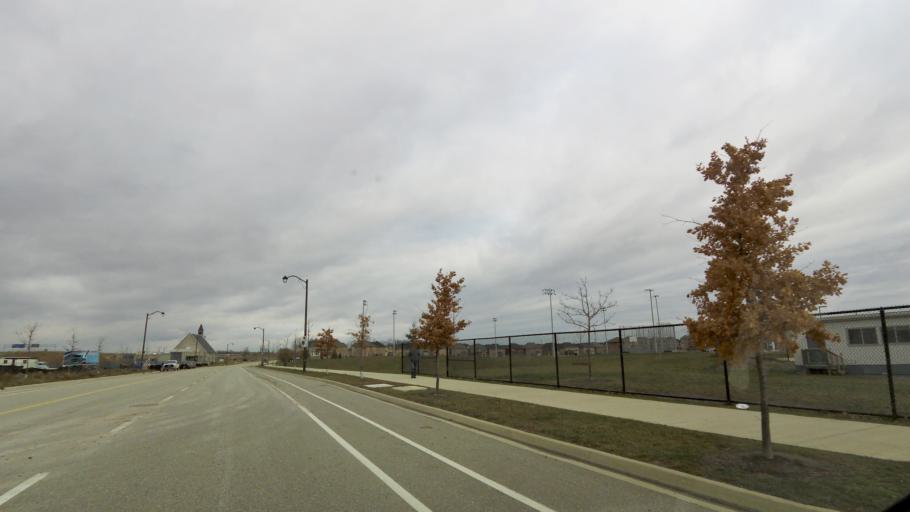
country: CA
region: Ontario
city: Burlington
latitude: 43.4078
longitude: -79.8252
